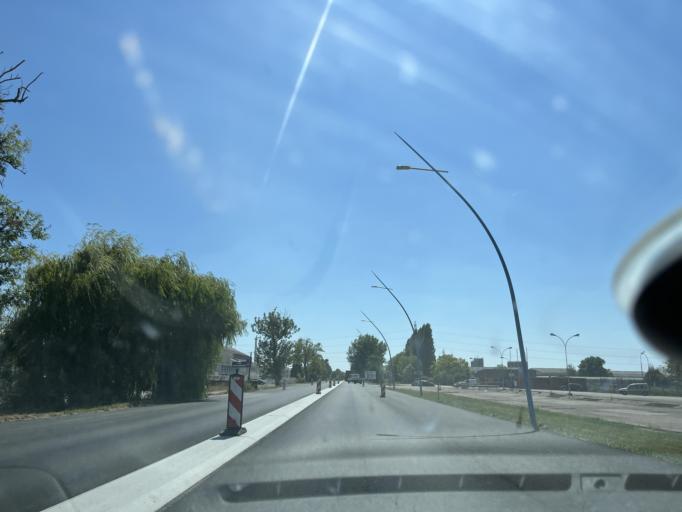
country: FR
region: Haute-Normandie
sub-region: Departement de la Seine-Maritime
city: Lillebonne
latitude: 49.4969
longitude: 0.5355
